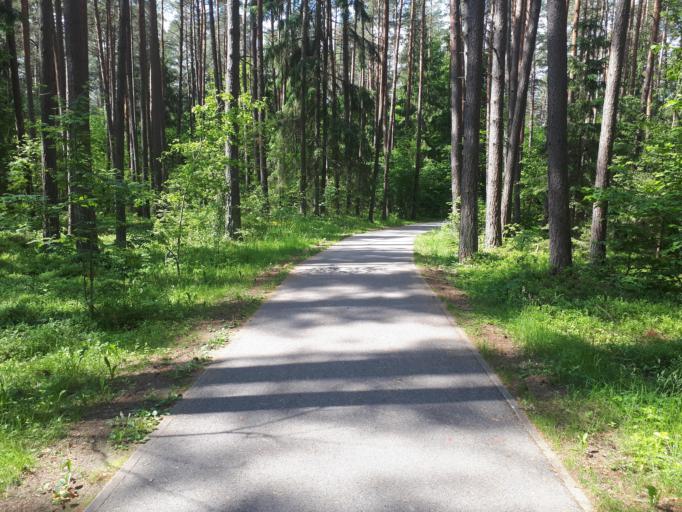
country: LT
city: Prienai
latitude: 54.6336
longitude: 23.9658
